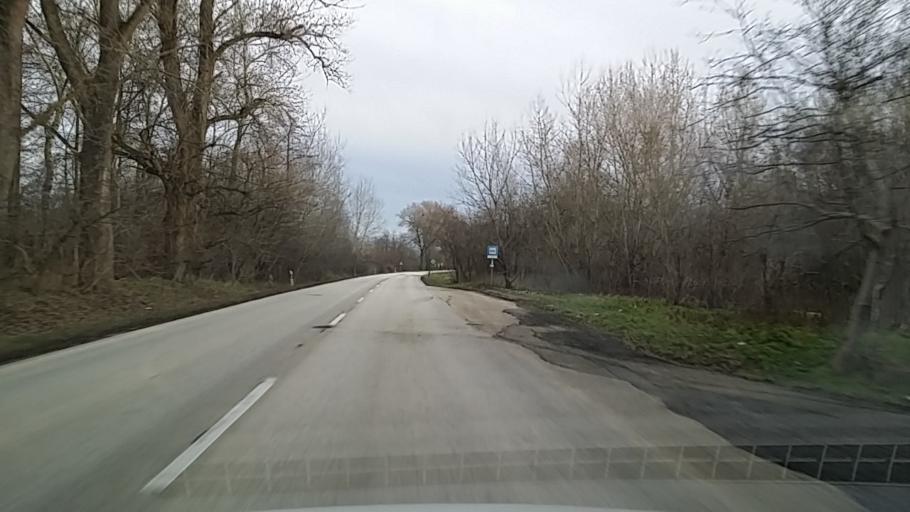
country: HU
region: Fejer
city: Mor
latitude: 47.4050
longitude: 18.1614
